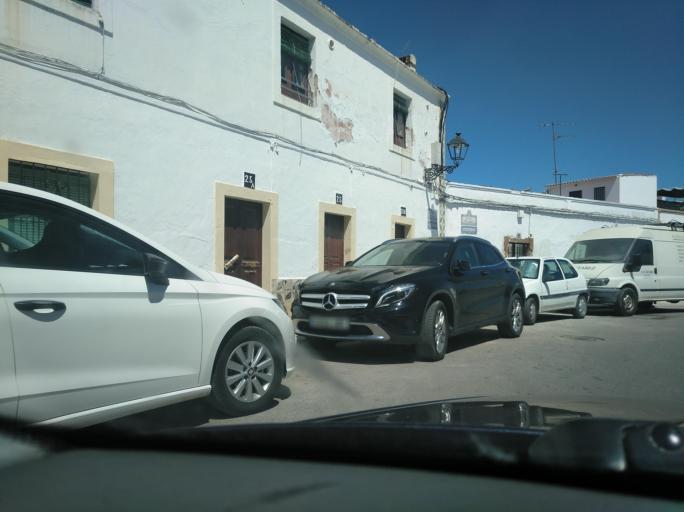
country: ES
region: Extremadura
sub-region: Provincia de Badajoz
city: Olivenza
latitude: 38.6870
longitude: -7.1021
